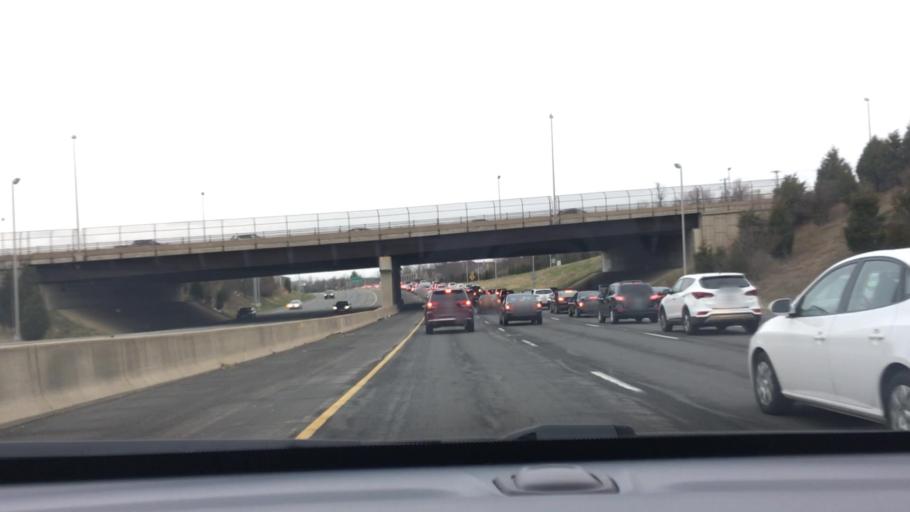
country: US
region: Virginia
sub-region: Fairfax County
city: Centreville
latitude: 38.8377
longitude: -77.4317
